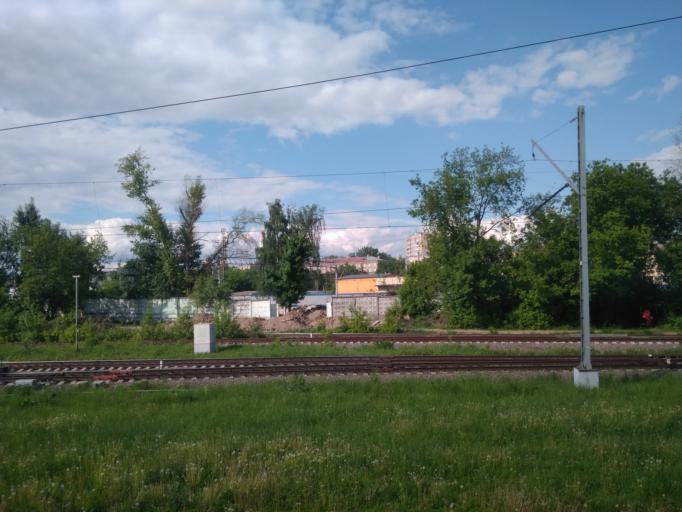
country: RU
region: Moscow
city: Mar'ina Roshcha
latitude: 55.8009
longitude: 37.6269
